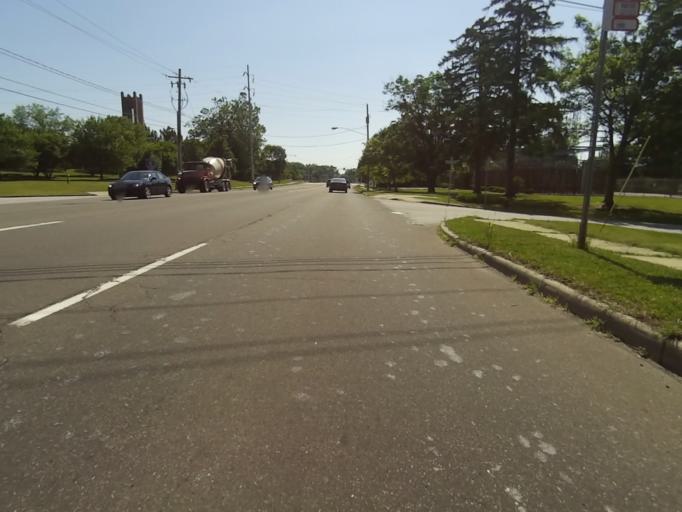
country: US
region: Ohio
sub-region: Summit County
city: Stow
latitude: 41.1667
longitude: -81.4440
